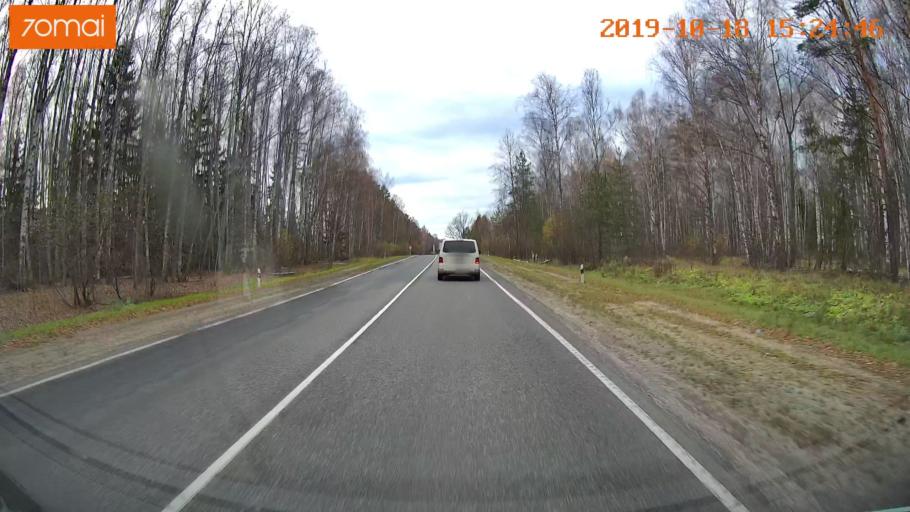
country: RU
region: Vladimir
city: Anopino
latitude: 55.7371
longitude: 40.7179
